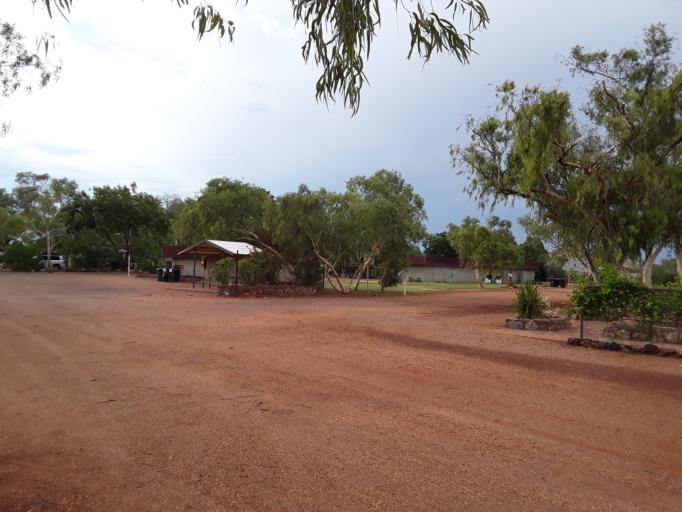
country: AU
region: Northern Territory
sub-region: Barkly
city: Tennant Creek
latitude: -19.6389
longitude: 134.1931
